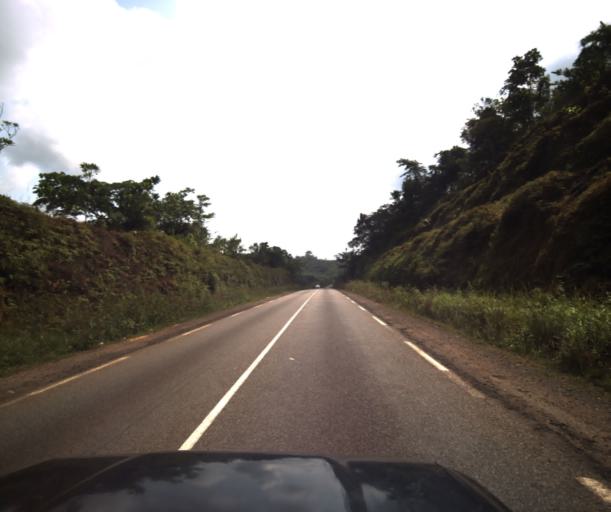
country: CM
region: Littoral
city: Edea
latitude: 3.8001
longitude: 10.2230
